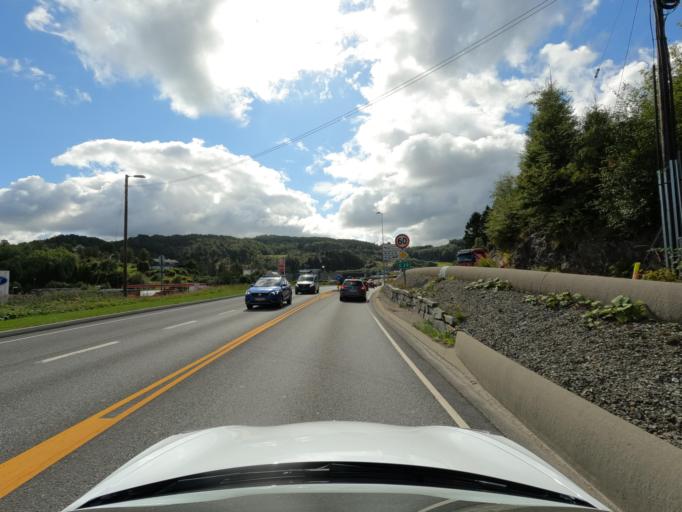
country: NO
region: Hordaland
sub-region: Bergen
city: Hylkje
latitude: 60.4856
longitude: 5.3760
